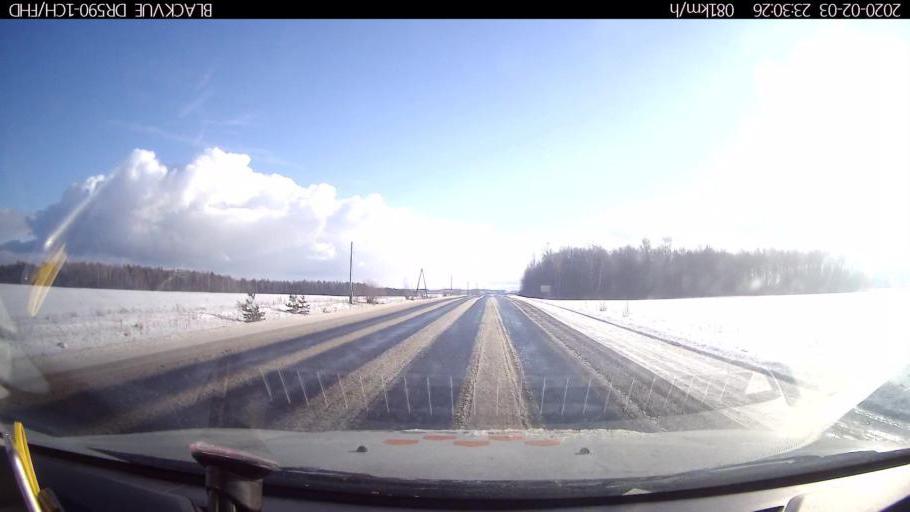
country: RU
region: Nizjnij Novgorod
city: Dal'neye Konstantinovo
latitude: 55.9525
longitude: 44.2153
